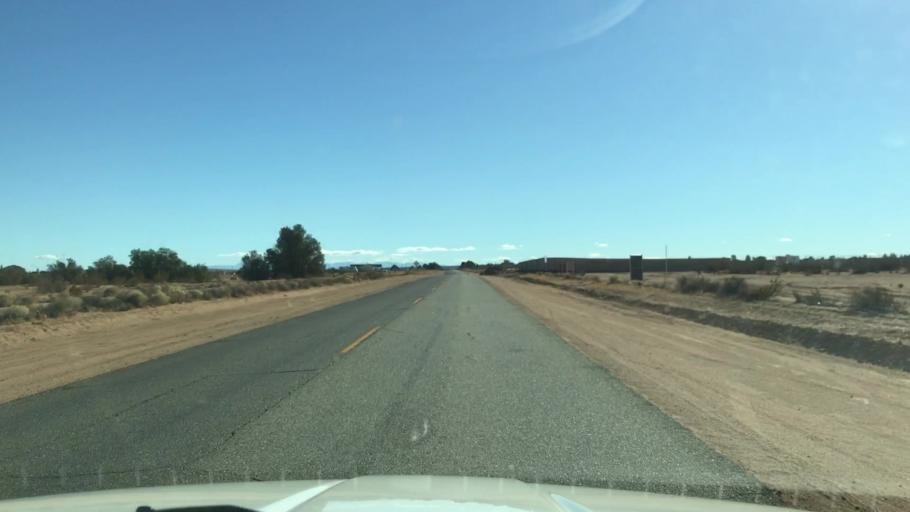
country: US
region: California
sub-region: Kern County
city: California City
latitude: 35.1427
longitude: -117.9859
